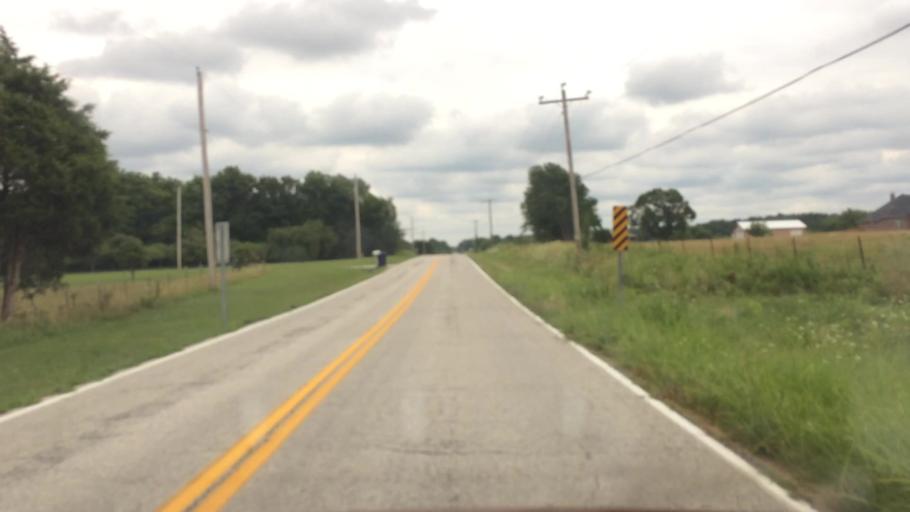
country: US
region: Missouri
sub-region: Greene County
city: Strafford
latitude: 37.2943
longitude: -93.2153
